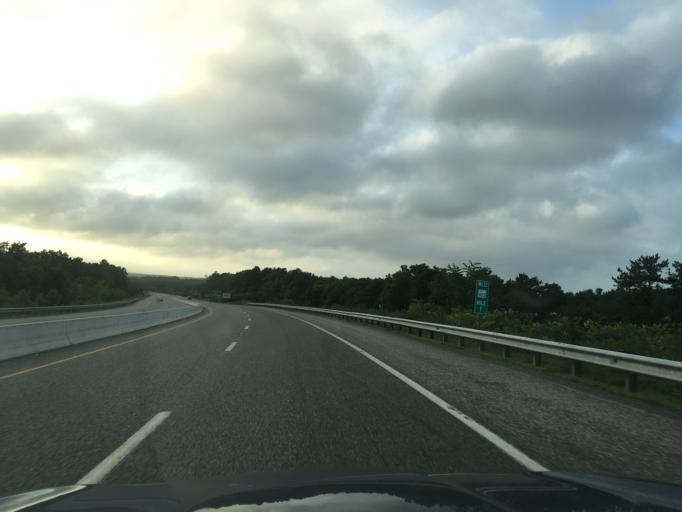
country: US
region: Rhode Island
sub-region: Kent County
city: East Greenwich
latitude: 41.6222
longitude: -71.4720
